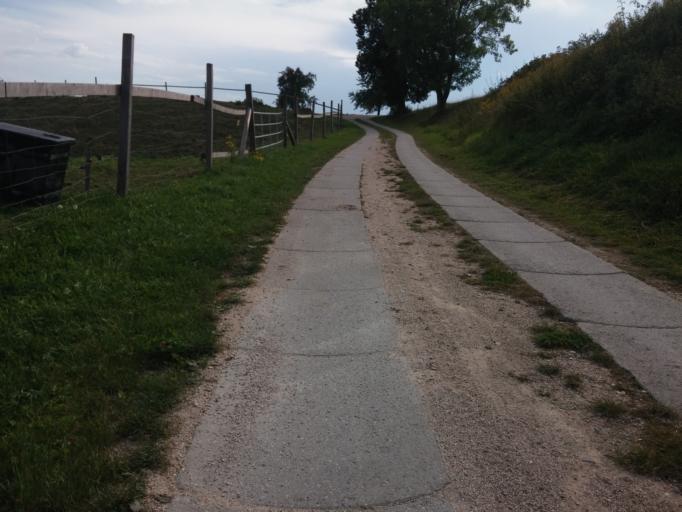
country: DE
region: Baden-Wuerttemberg
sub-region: Tuebingen Region
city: Herbertingen
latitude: 48.0940
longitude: 9.4096
